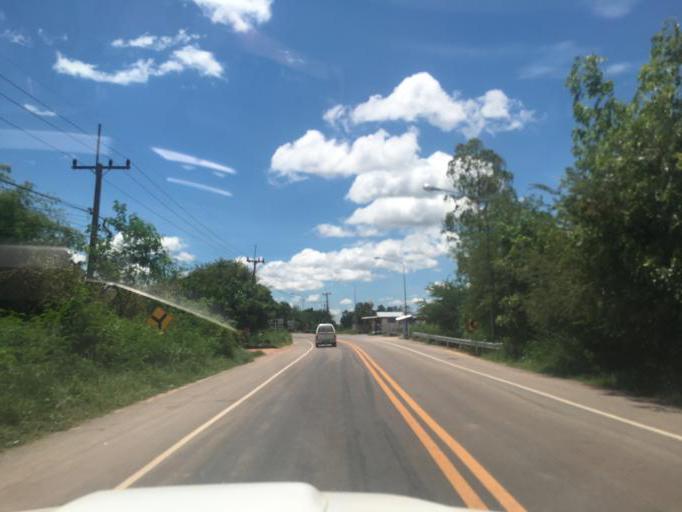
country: TH
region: Changwat Udon Thani
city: Nong Saeng
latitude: 17.2265
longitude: 102.7384
